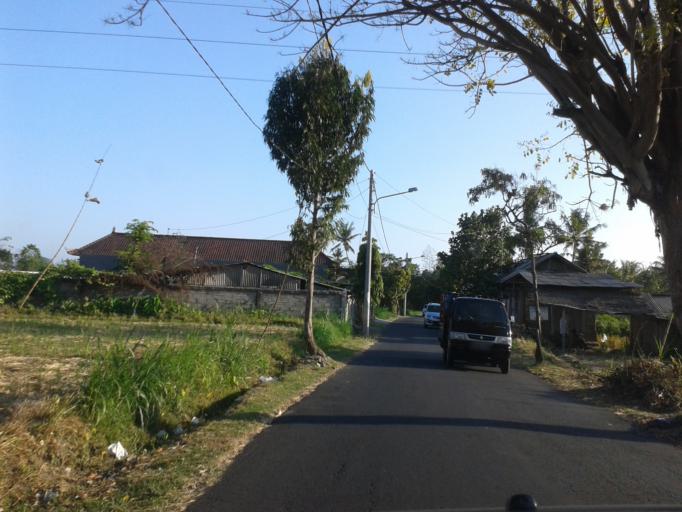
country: ID
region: Bali
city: Semarapura
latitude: -8.5626
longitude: 115.3866
